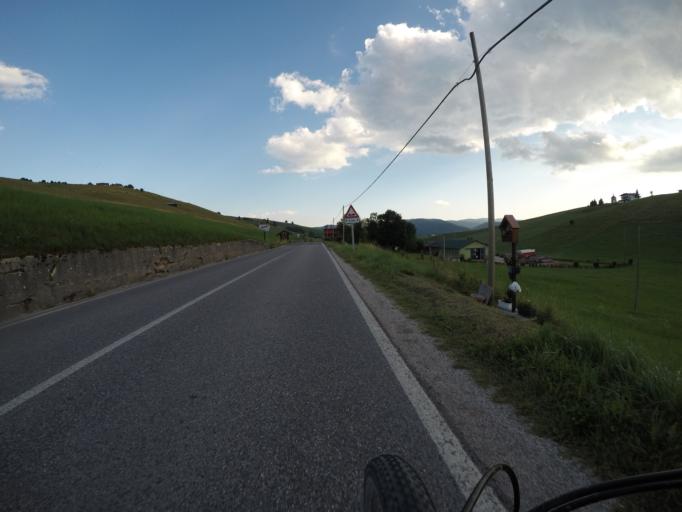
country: IT
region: Veneto
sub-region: Provincia di Vicenza
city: Gallio
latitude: 45.8831
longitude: 11.5480
